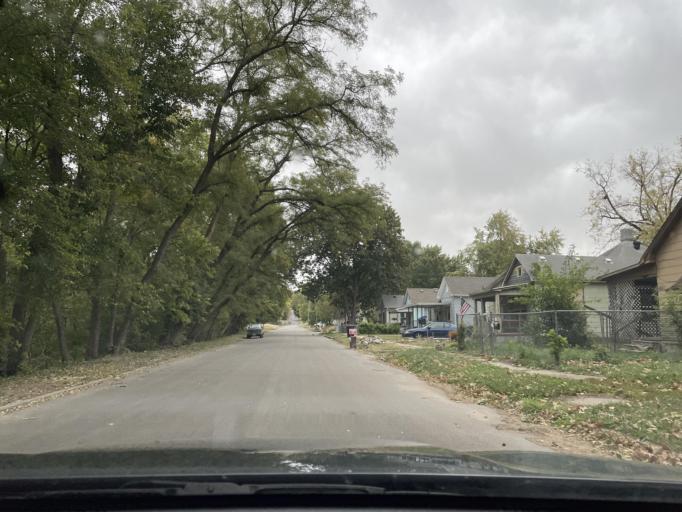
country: US
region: Missouri
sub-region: Buchanan County
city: Saint Joseph
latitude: 39.7788
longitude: -94.8415
